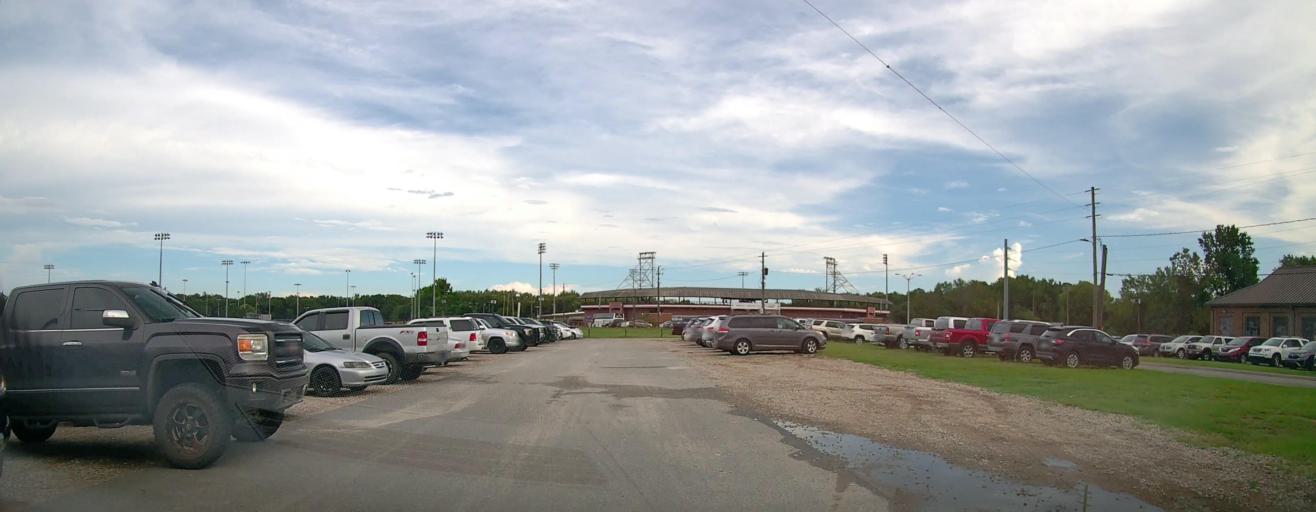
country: US
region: Georgia
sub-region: Bibb County
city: Macon
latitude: 32.8310
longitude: -83.6149
